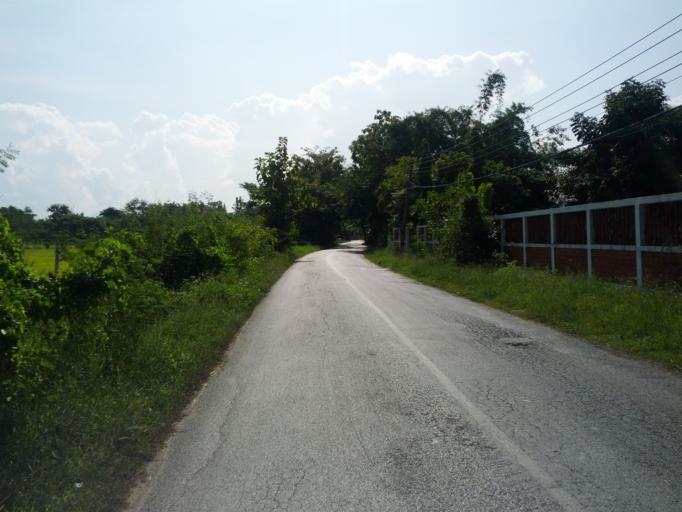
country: TH
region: Chiang Mai
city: San Kamphaeng
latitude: 18.7645
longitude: 99.1137
